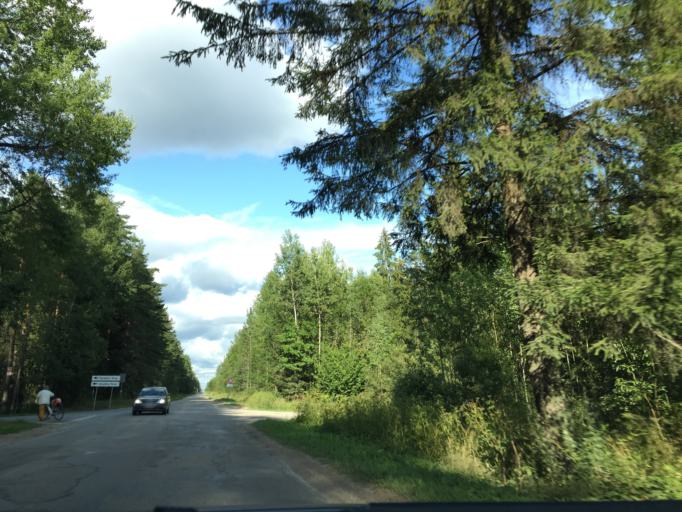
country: LV
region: Ogre
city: Ogre
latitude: 56.8290
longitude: 24.6444
